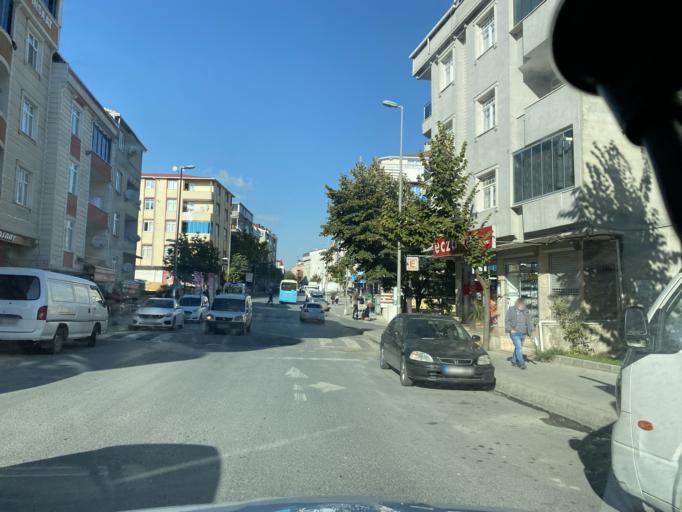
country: TR
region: Istanbul
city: Esenyurt
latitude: 41.0425
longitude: 28.6502
